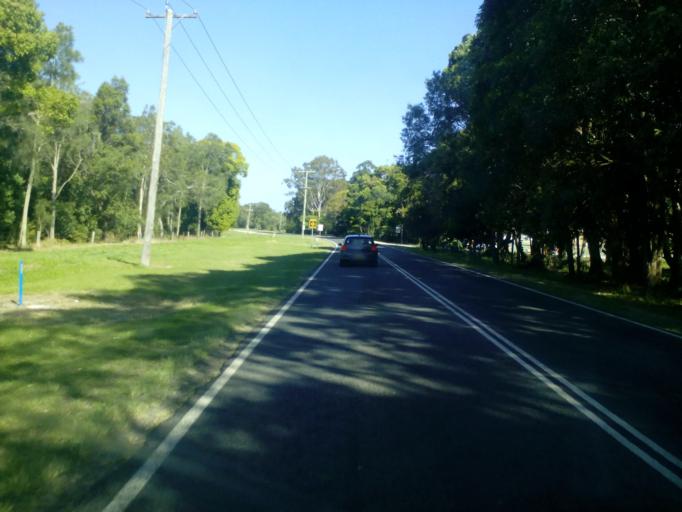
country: AU
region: New South Wales
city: Chinderah
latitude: -28.2489
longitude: 153.5554
